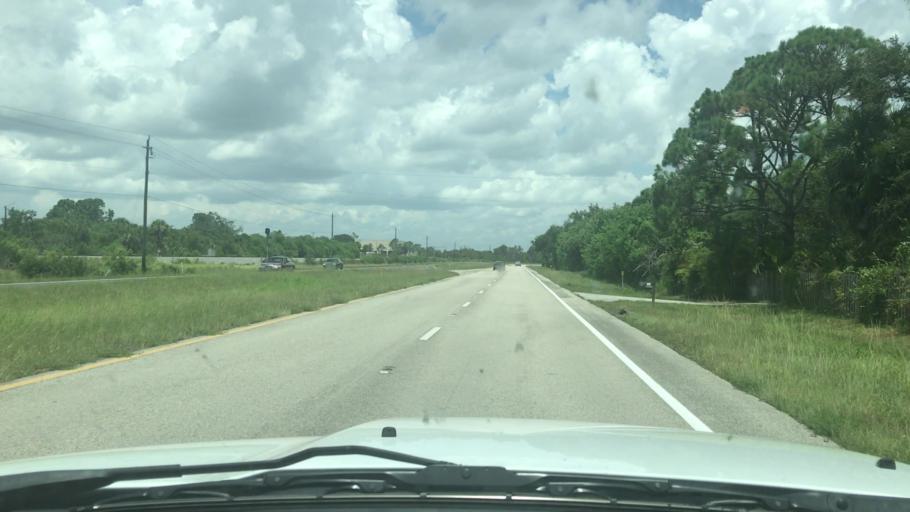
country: US
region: Florida
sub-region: Brevard County
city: Malabar
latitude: 27.9765
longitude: -80.5509
